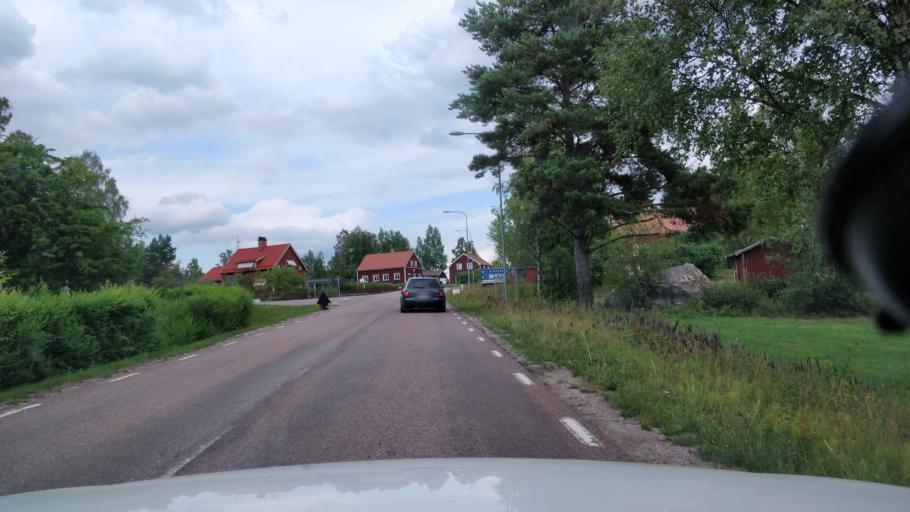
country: SE
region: Dalarna
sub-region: Faluns Kommun
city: Bjursas
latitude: 60.7448
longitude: 15.4692
